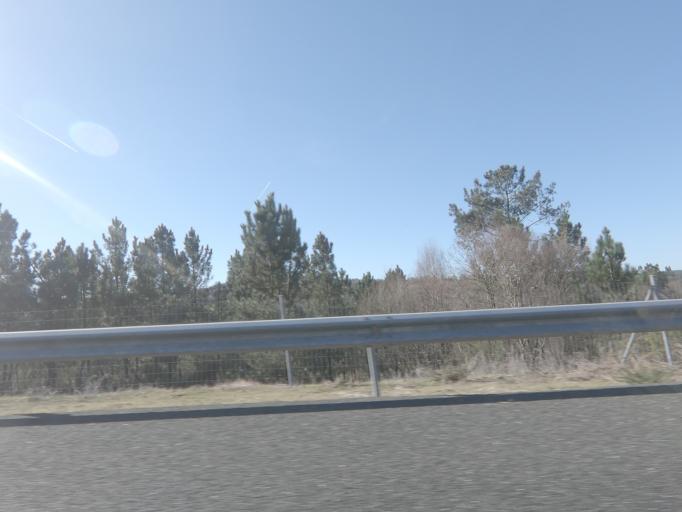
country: ES
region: Galicia
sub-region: Provincia de Pontevedra
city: Lalin
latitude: 42.6023
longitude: -8.0970
